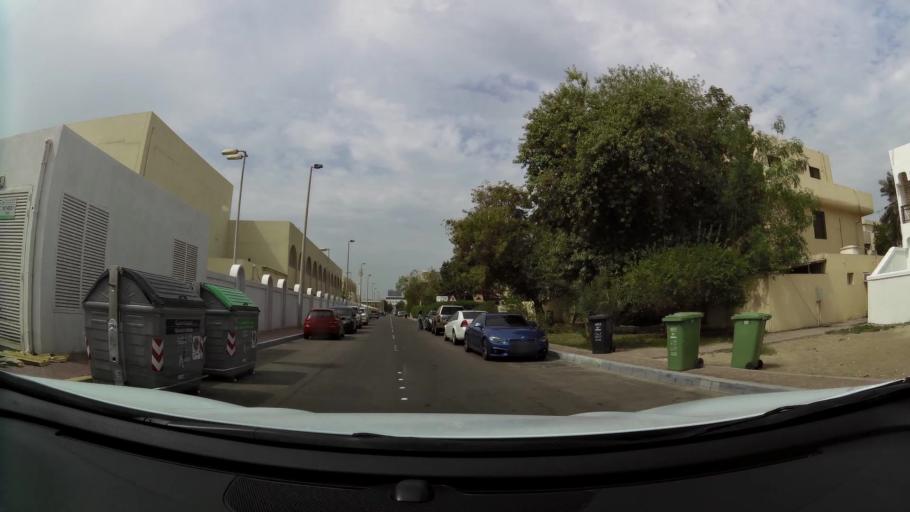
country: AE
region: Abu Dhabi
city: Abu Dhabi
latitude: 24.4595
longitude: 54.3692
